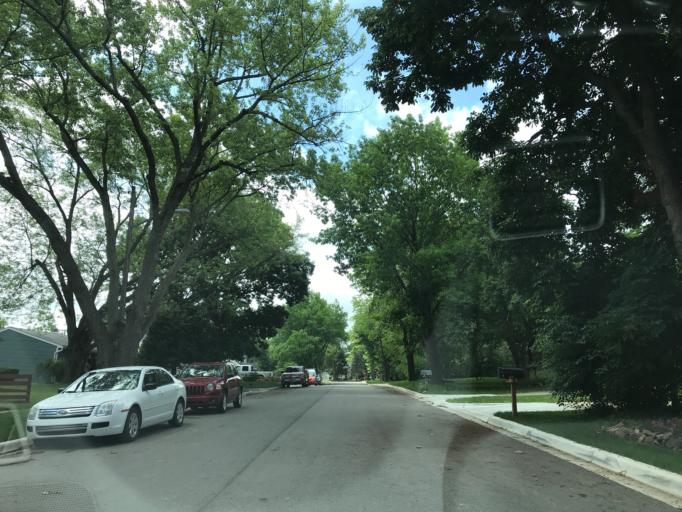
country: US
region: Michigan
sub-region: Washtenaw County
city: Ann Arbor
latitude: 42.2417
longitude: -83.7037
